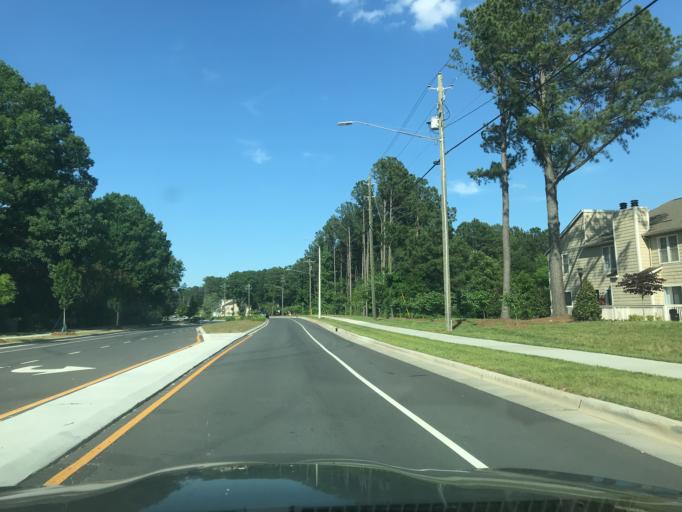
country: US
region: North Carolina
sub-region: Wake County
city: West Raleigh
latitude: 35.8681
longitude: -78.6323
